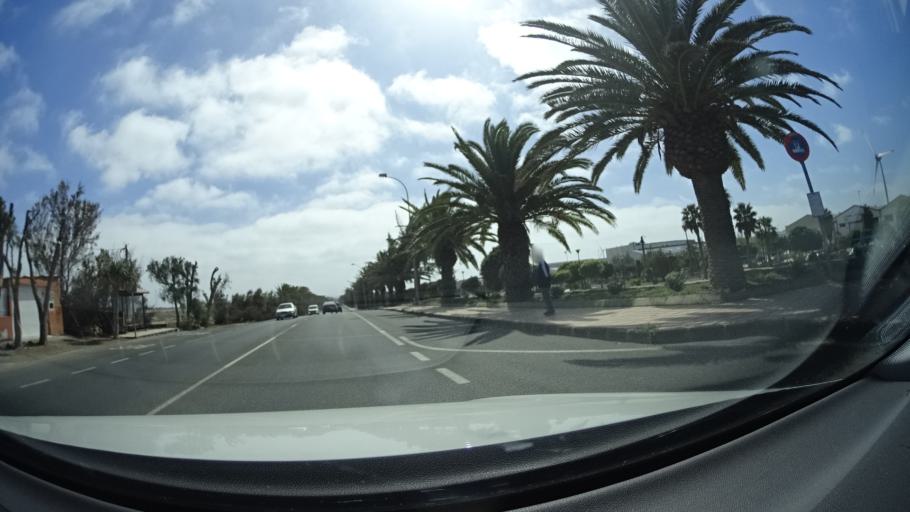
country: ES
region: Canary Islands
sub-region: Provincia de Las Palmas
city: Cruce de Arinaga
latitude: 27.8620
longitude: -15.4038
